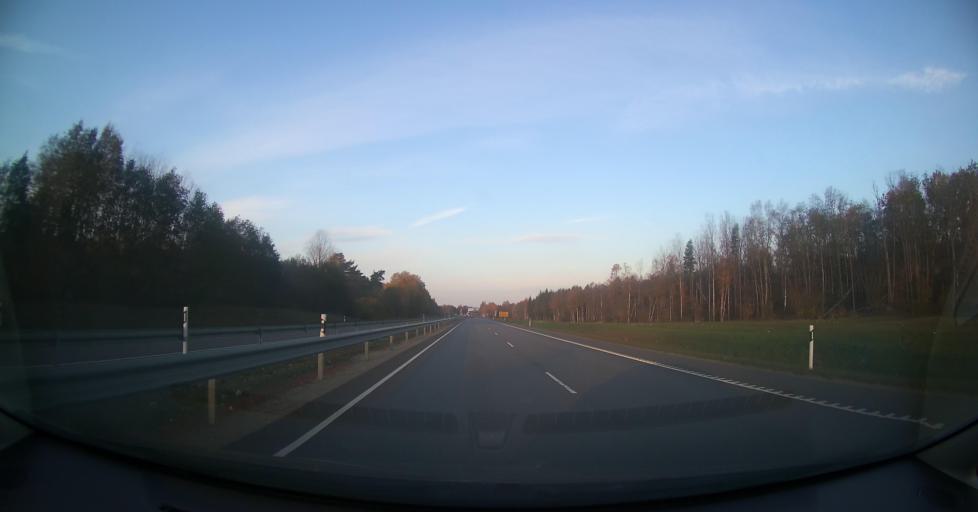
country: EE
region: Harju
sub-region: Saue vald
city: Laagri
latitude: 59.3131
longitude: 24.5964
